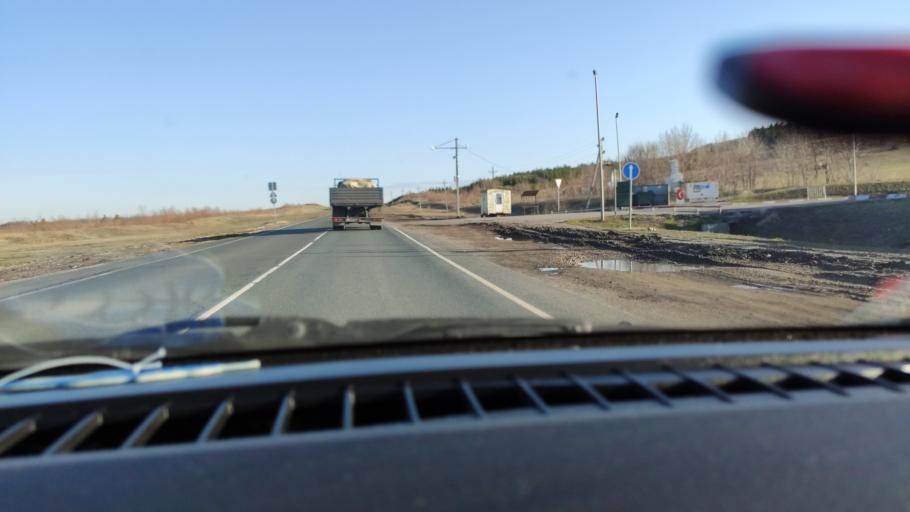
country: RU
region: Saratov
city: Alekseyevka
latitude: 52.2960
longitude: 47.9286
